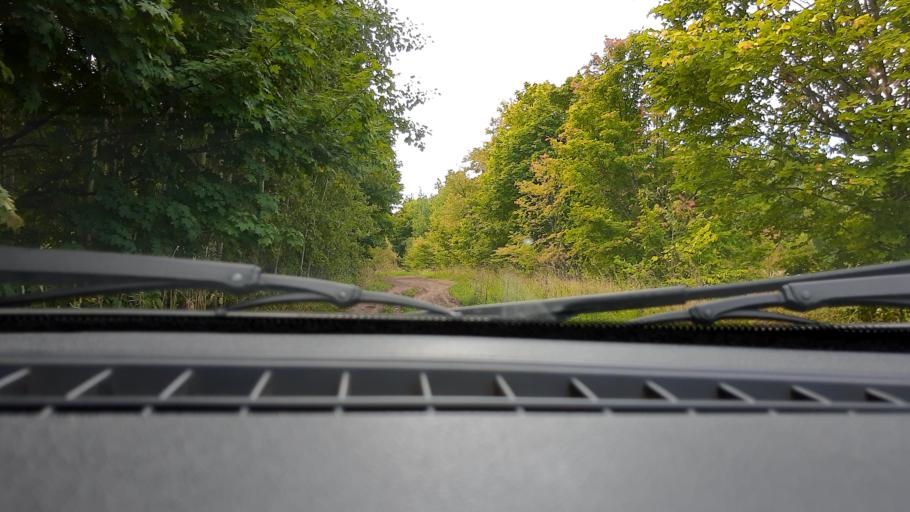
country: RU
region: Bashkortostan
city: Avdon
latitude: 54.8125
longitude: 55.7342
